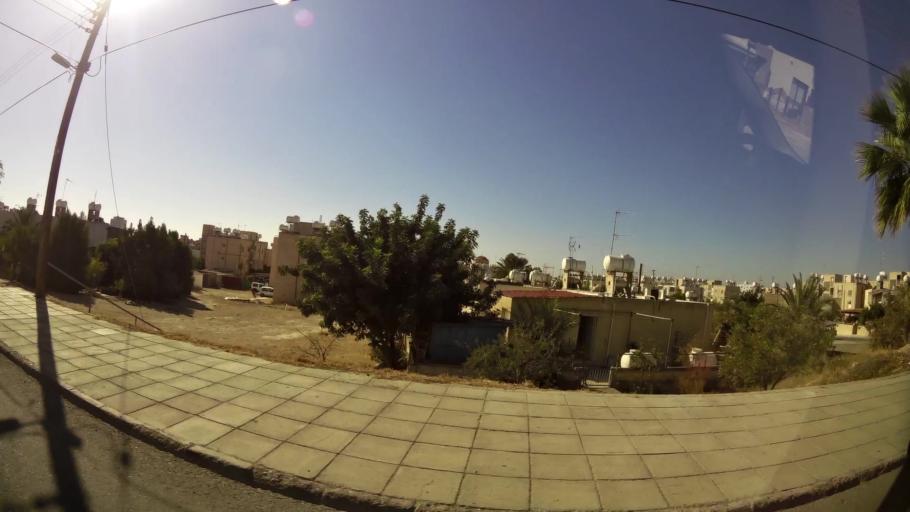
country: CY
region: Larnaka
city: Larnaca
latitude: 34.9371
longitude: 33.6246
